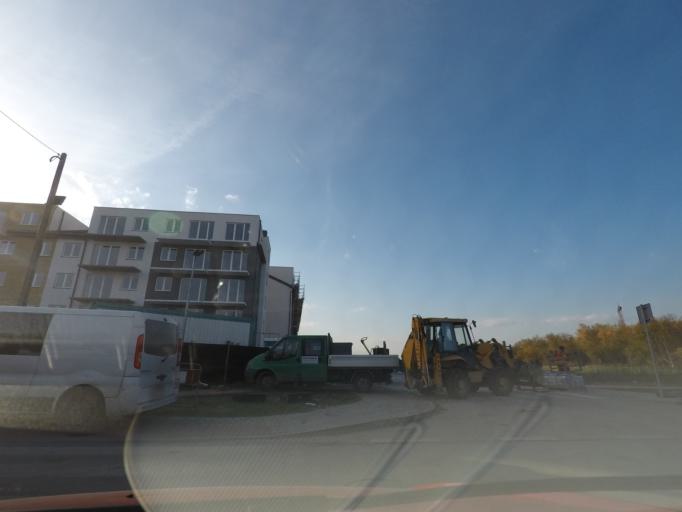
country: PL
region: Lesser Poland Voivodeship
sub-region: Powiat wielicki
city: Czarnochowice
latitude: 50.0238
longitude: 20.0513
